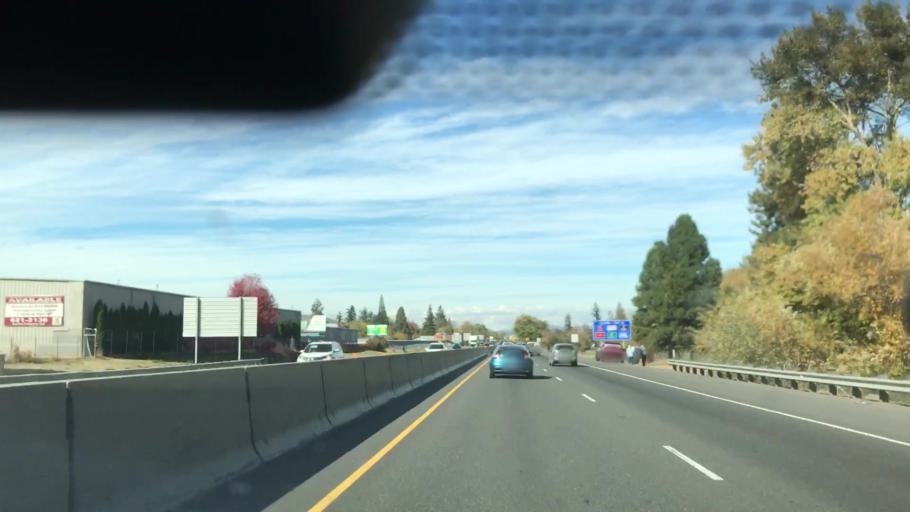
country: US
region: Oregon
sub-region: Jackson County
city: Medford
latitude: 42.3188
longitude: -122.8593
